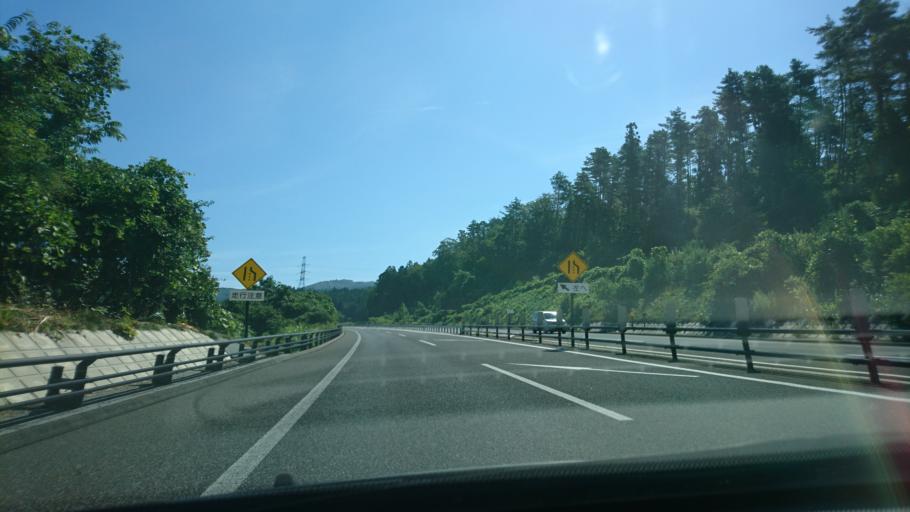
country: JP
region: Iwate
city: Kitakami
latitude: 39.2896
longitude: 141.2802
